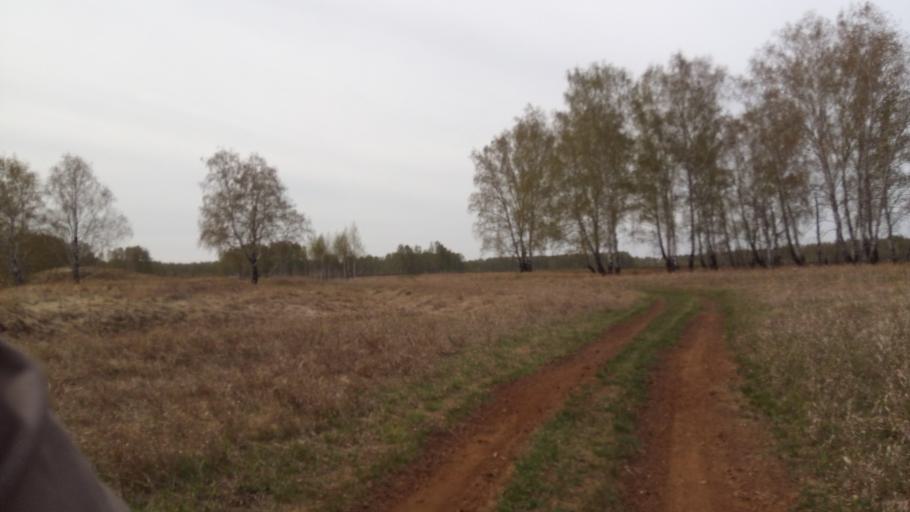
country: RU
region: Chelyabinsk
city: Timiryazevskiy
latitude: 55.0125
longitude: 60.8594
